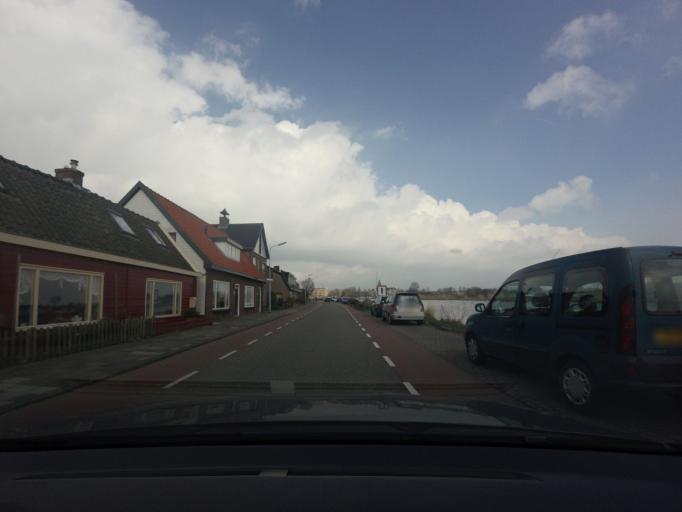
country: NL
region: North Holland
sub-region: Gemeente Zaanstad
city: Zaandam
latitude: 52.3763
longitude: 4.7571
